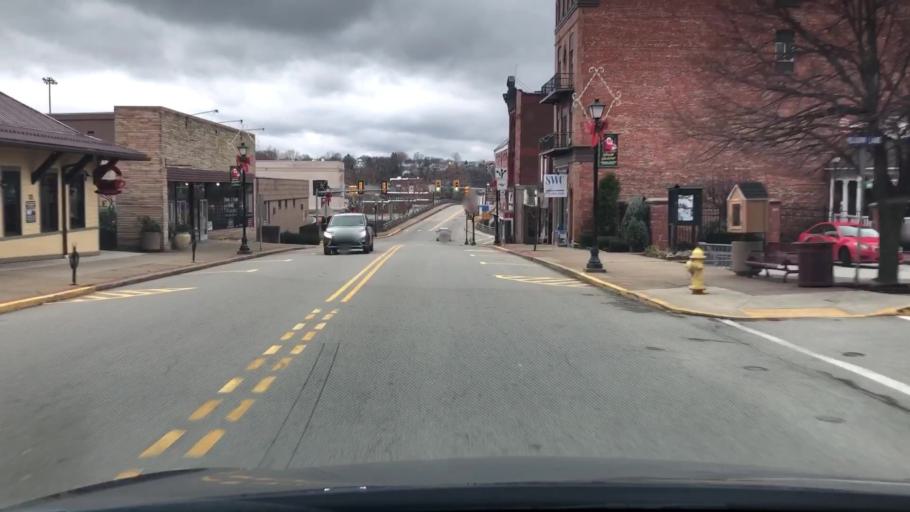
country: US
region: Pennsylvania
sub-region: Fayette County
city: Connellsville
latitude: 40.0176
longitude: -79.5903
